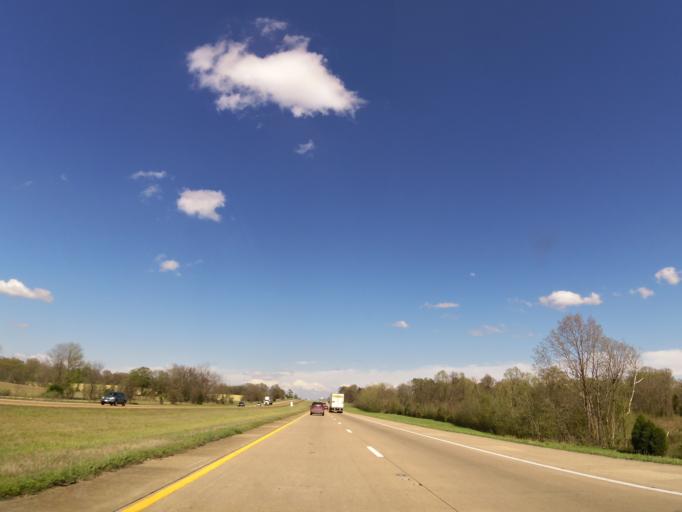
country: US
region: Tennessee
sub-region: Gibson County
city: Medina
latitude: 35.6966
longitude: -88.6957
